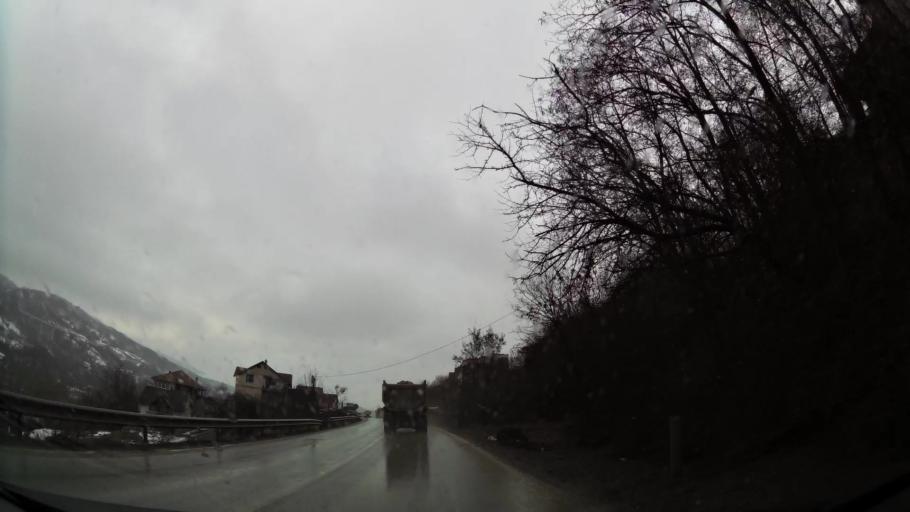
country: XK
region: Ferizaj
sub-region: Komuna e Kacanikut
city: Kacanik
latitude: 42.2328
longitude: 21.2529
